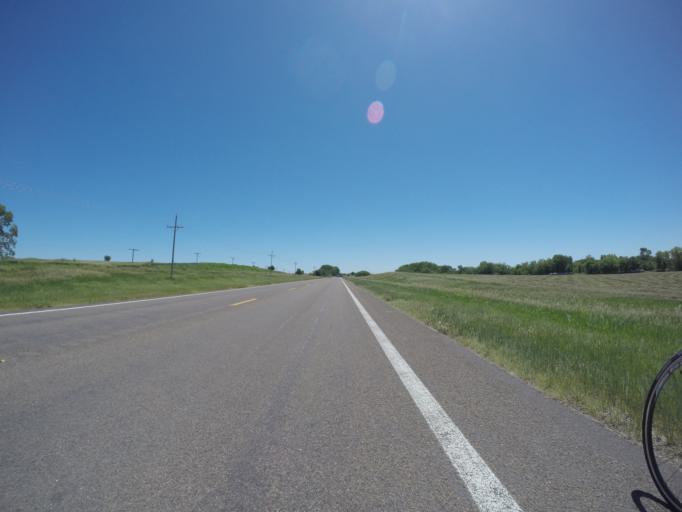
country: US
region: Kansas
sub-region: Phillips County
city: Phillipsburg
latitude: 39.8074
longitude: -99.4894
